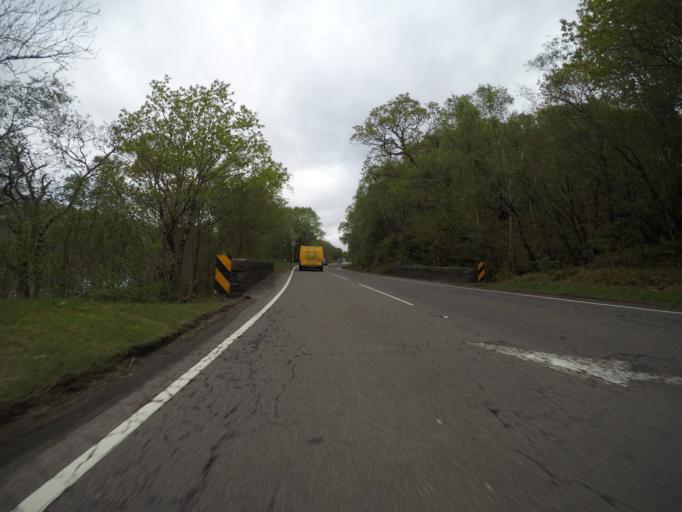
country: GB
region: Scotland
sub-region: Highland
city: Fort William
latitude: 56.7612
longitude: -5.1816
